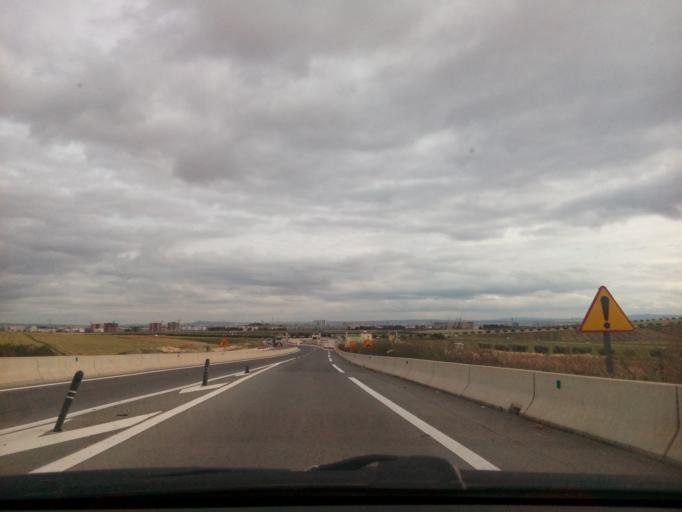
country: DZ
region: Sidi Bel Abbes
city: Sidi Bel Abbes
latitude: 35.2179
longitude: -0.6727
